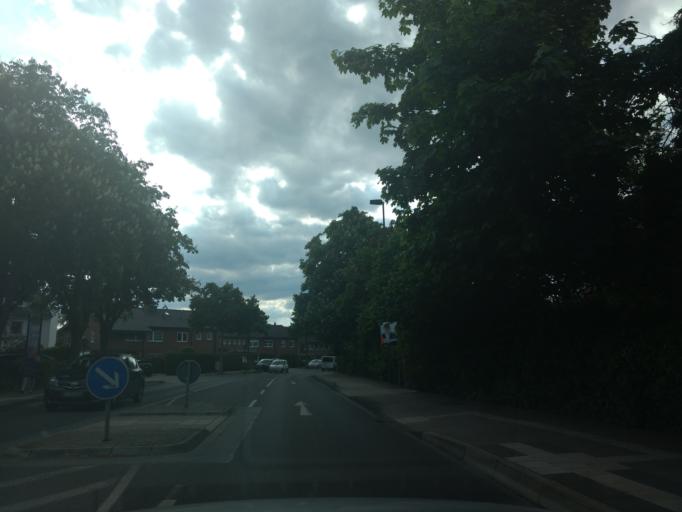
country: DE
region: North Rhine-Westphalia
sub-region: Regierungsbezirk Dusseldorf
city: Meerbusch
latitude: 51.2537
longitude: 6.7062
